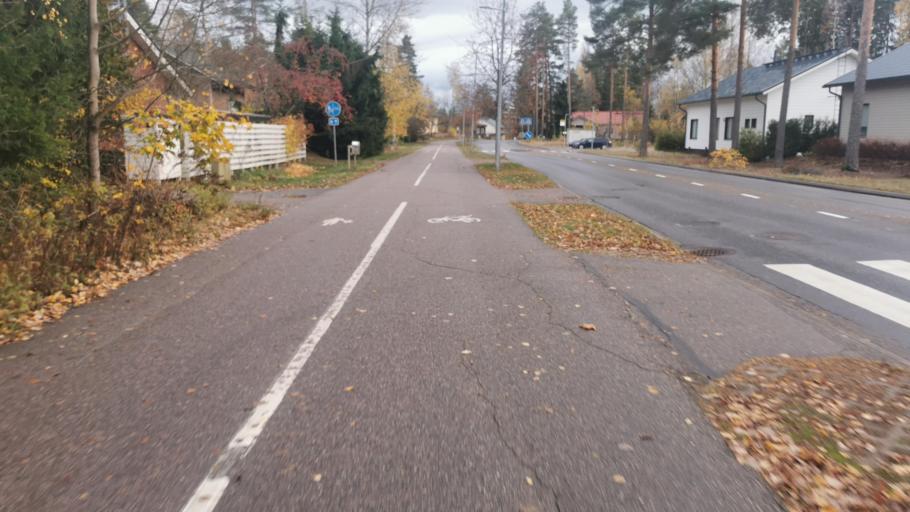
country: FI
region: Uusimaa
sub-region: Helsinki
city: Kerava
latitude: 60.4136
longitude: 25.0823
